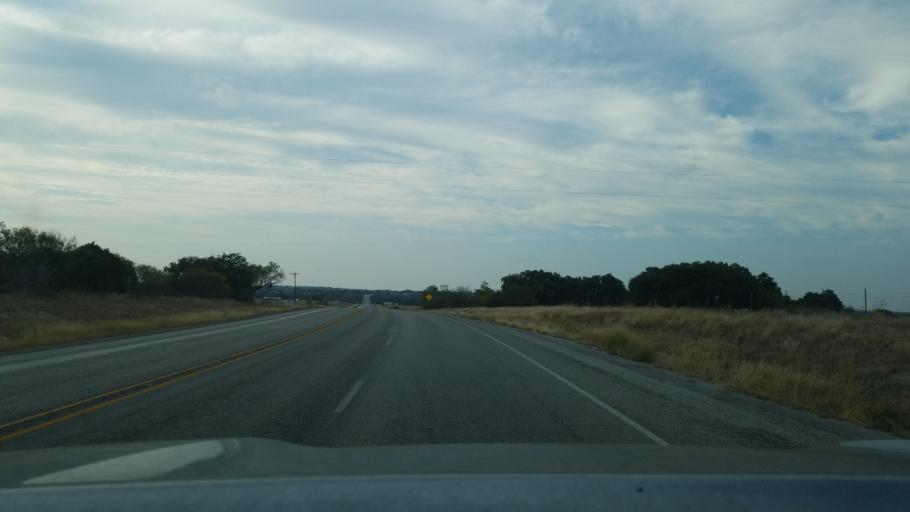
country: US
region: Texas
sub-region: Mills County
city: Goldthwaite
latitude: 31.5464
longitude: -98.6341
